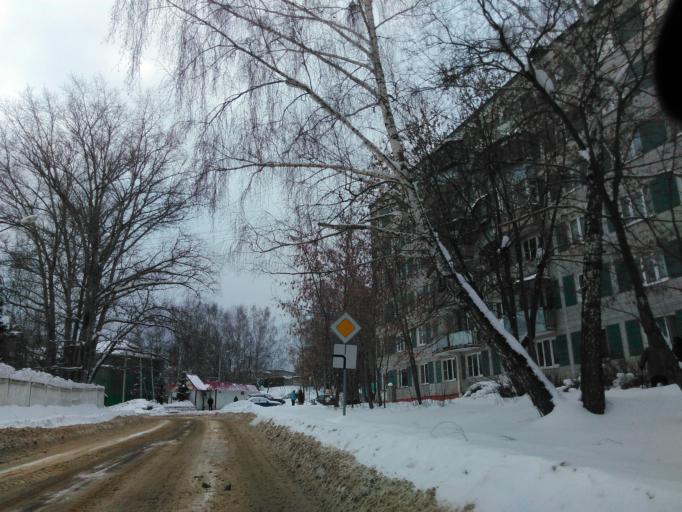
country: RU
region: Moskovskaya
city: Yakhroma
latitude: 56.2805
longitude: 37.4844
